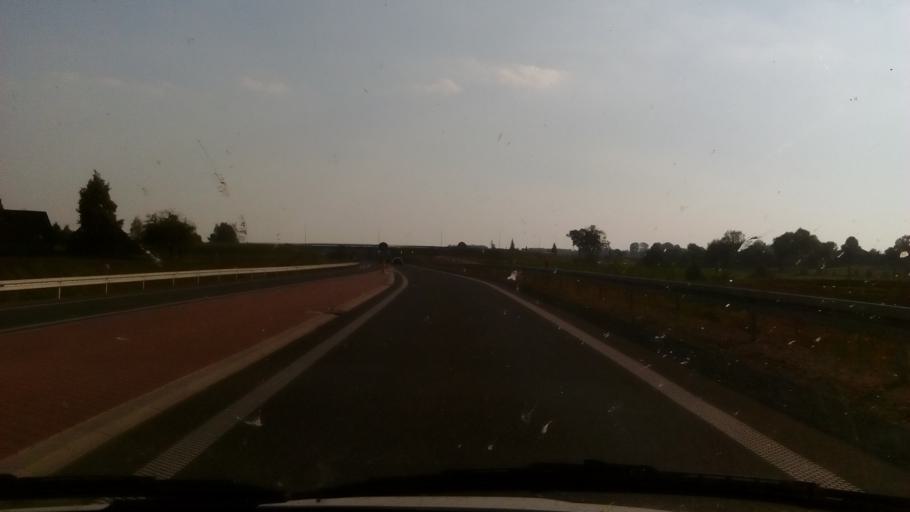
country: PL
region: Podlasie
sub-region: Powiat grajewski
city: Rajgrod
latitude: 53.7774
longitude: 22.8369
